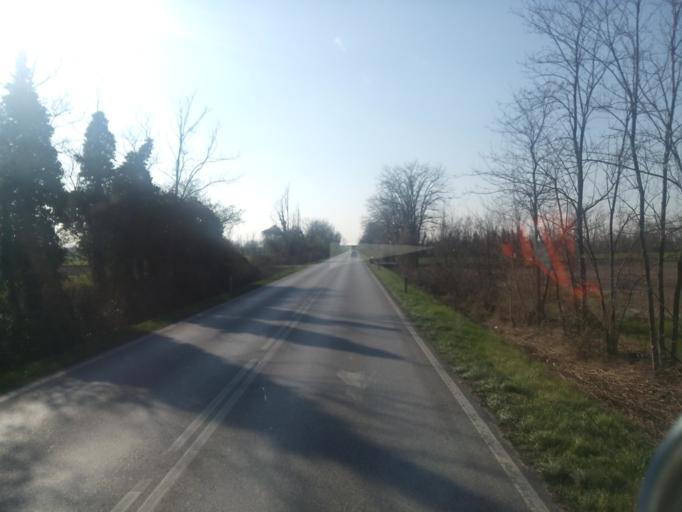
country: IT
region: Friuli Venezia Giulia
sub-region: Provincia di Udine
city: Talmassons
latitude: 45.9433
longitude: 13.0981
